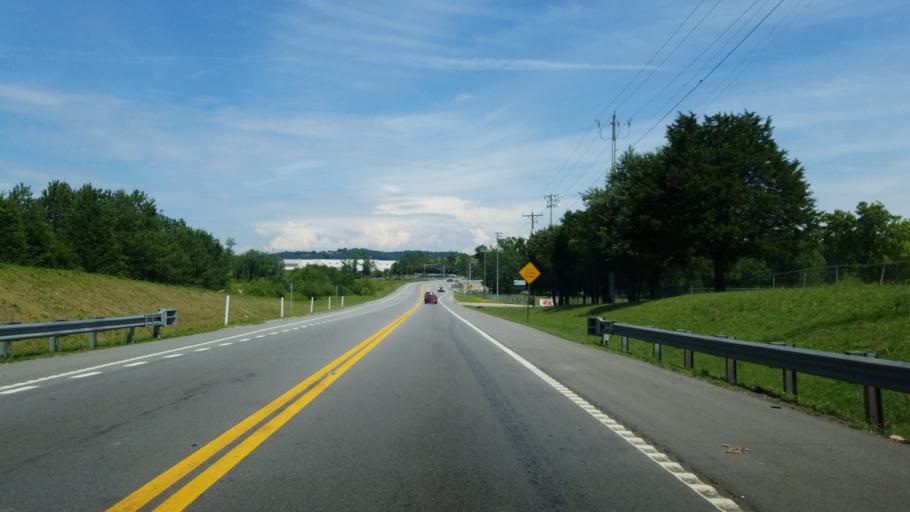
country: US
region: Tennessee
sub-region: Hamilton County
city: Harrison
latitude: 35.0703
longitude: -85.1521
